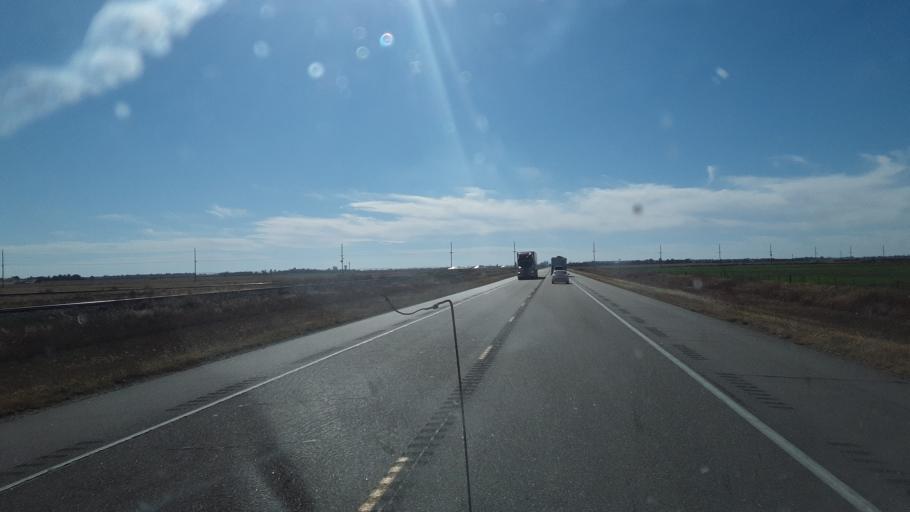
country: US
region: Kansas
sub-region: Pawnee County
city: Larned
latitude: 38.2209
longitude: -99.0442
